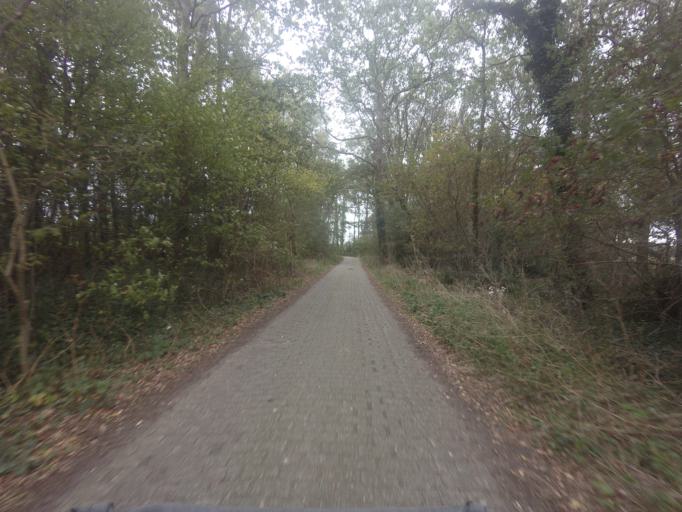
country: NL
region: Friesland
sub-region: Gemeente Weststellingwerf
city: Noordwolde
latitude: 52.9324
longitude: 6.1769
